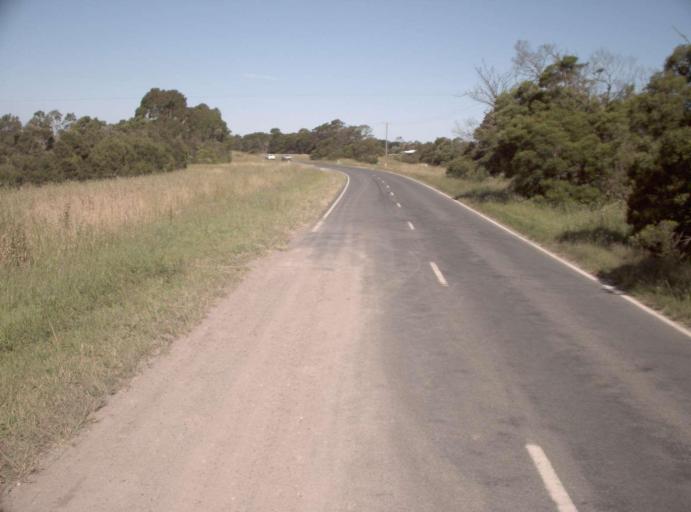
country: AU
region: Victoria
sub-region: Latrobe
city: Traralgon
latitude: -38.6251
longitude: 146.6483
